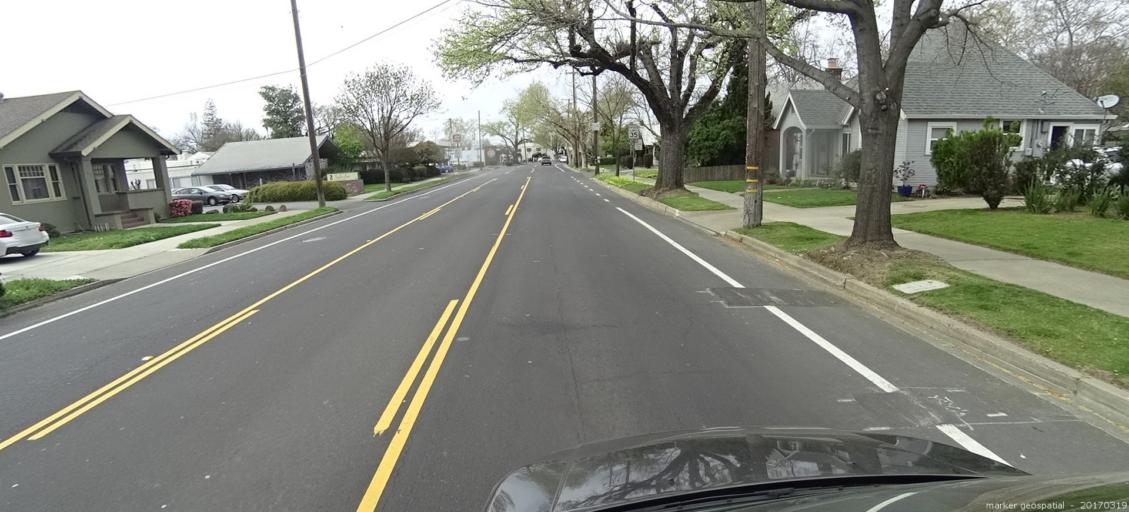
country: US
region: California
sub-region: Sacramento County
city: Sacramento
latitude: 38.5663
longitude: -121.4617
